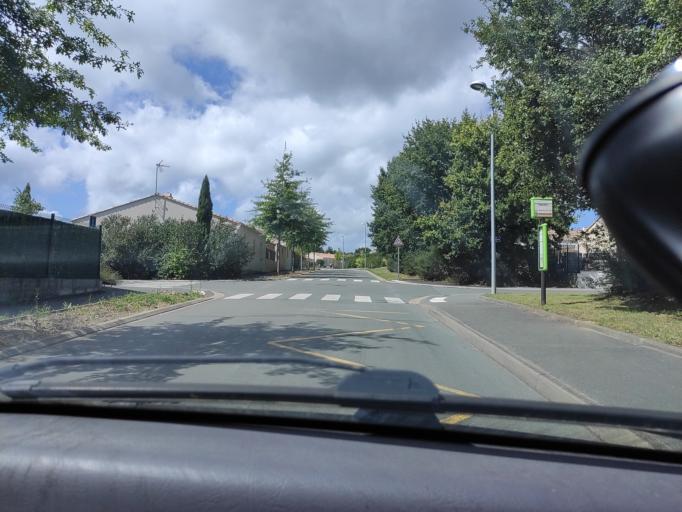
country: FR
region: Pays de la Loire
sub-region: Departement de la Vendee
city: La Roche-sur-Yon
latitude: 46.6901
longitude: -1.4497
